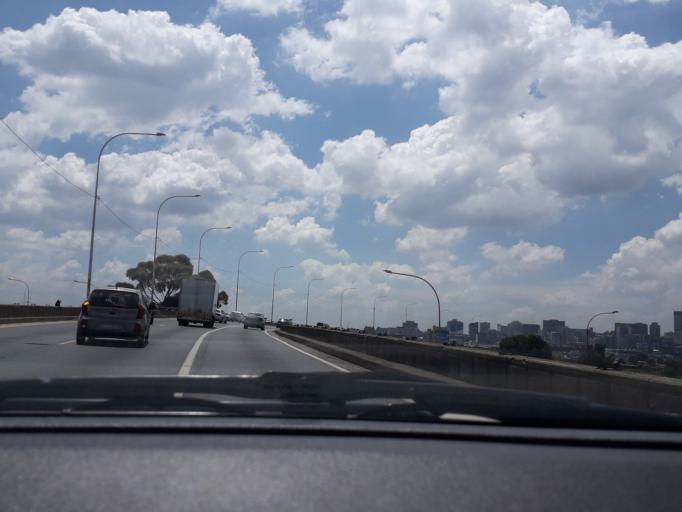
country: ZA
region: Gauteng
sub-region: City of Johannesburg Metropolitan Municipality
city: Johannesburg
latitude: -26.2149
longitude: 28.0234
